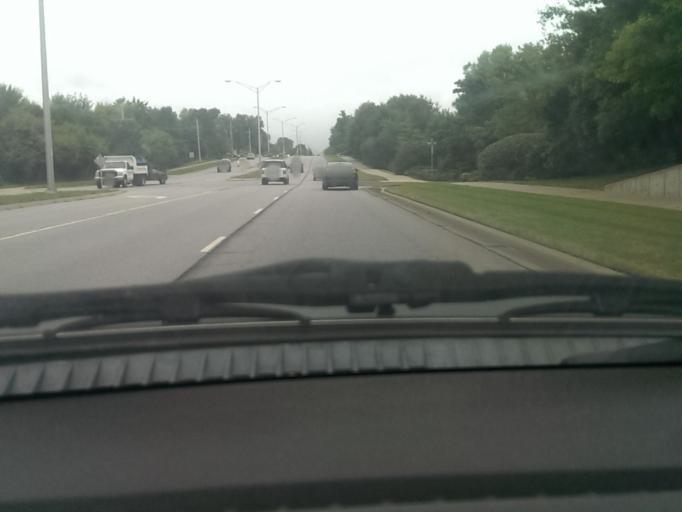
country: US
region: Kansas
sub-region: Johnson County
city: Leawood
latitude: 38.8948
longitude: -94.6493
